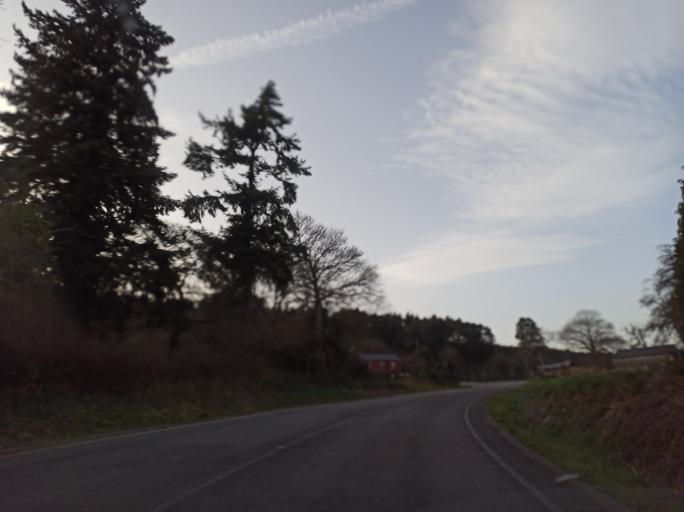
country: ES
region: Galicia
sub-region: Provincia de Lugo
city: Friol
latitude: 43.0255
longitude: -7.8799
